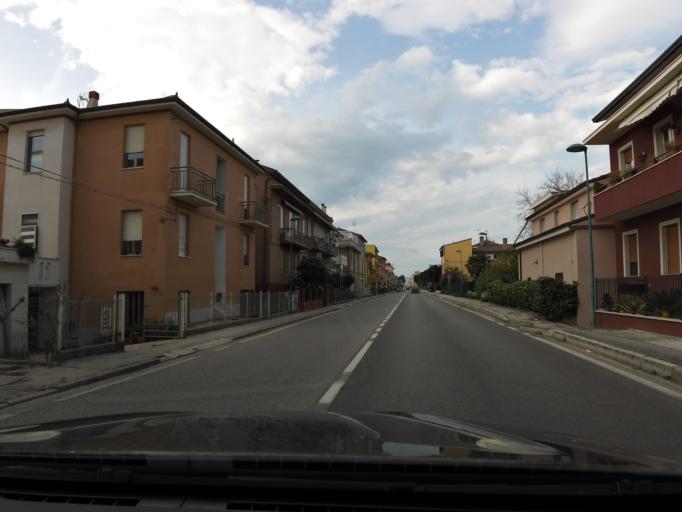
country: IT
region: The Marches
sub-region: Provincia di Macerata
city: Porto Potenza Picena
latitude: 43.3639
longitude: 13.6955
